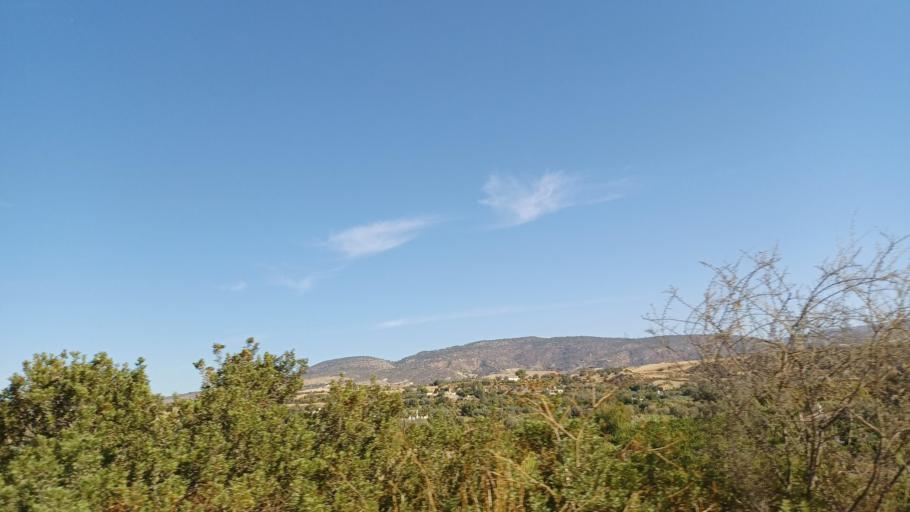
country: CY
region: Pafos
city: Polis
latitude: 34.9939
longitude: 32.4404
